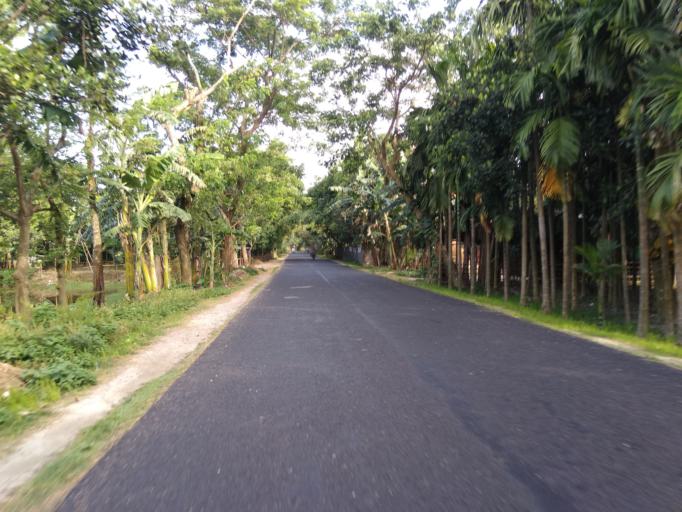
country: BD
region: Rangpur Division
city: Rangpur
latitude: 25.8368
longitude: 89.1146
